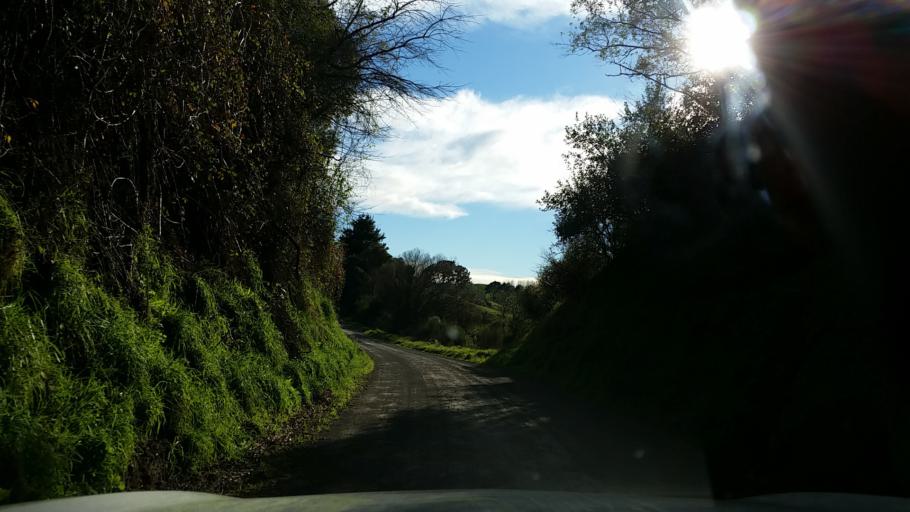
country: NZ
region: Waikato
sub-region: South Waikato District
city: Tokoroa
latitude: -38.3896
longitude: 176.0778
